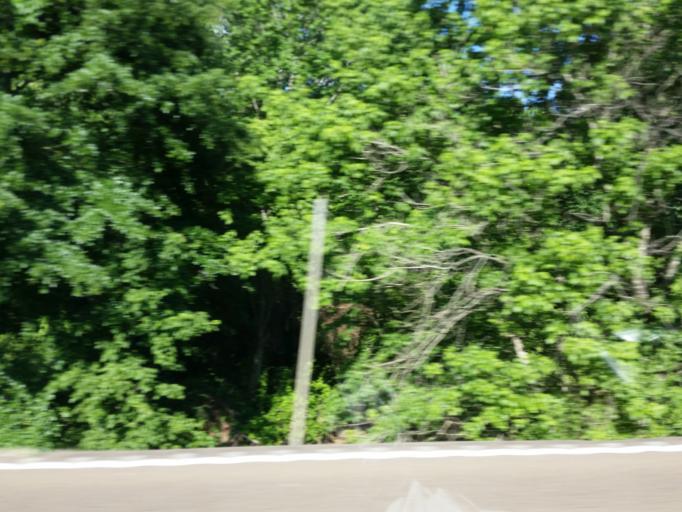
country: US
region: Mississippi
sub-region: Calhoun County
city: Calhoun City
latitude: 33.7737
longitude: -89.3640
